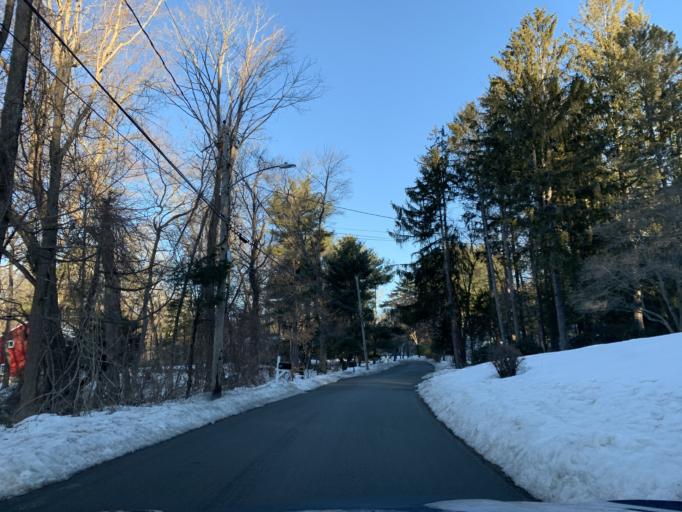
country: US
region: Massachusetts
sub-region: Norfolk County
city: Westwood
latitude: 42.2095
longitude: -71.2379
